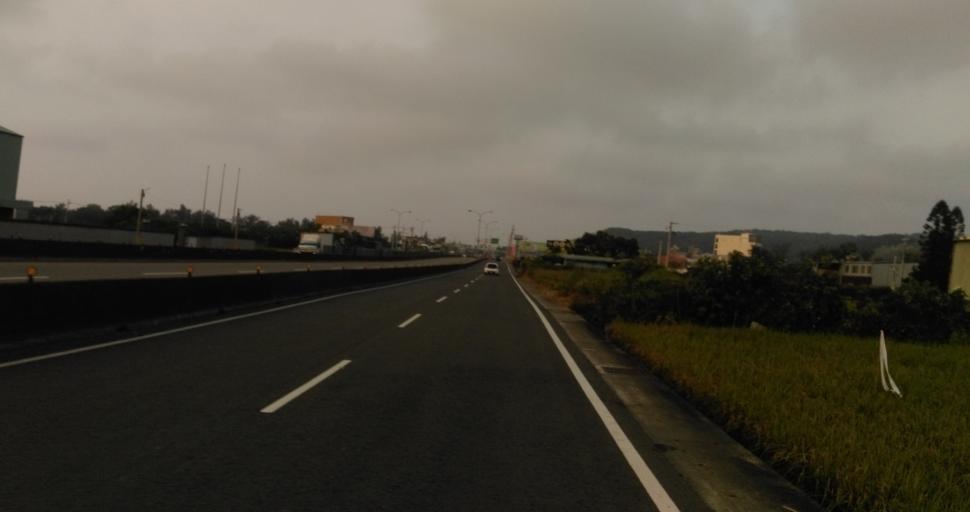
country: TW
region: Taiwan
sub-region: Hsinchu
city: Zhubei
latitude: 24.8689
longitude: 120.9536
